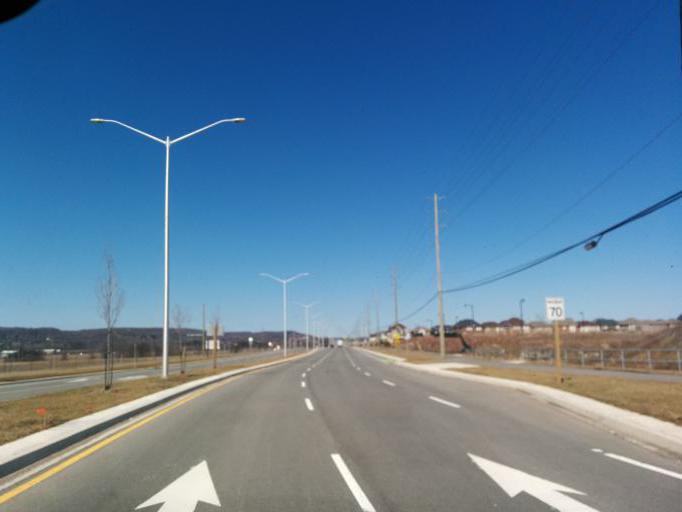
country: CA
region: Ontario
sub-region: Halton
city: Milton
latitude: 43.4768
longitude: -79.8707
